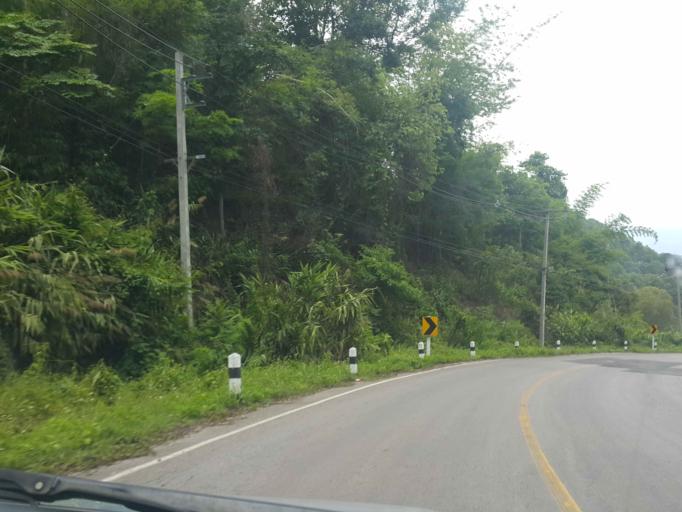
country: TH
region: Phayao
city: Chiang Muan
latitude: 18.9209
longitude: 100.1924
